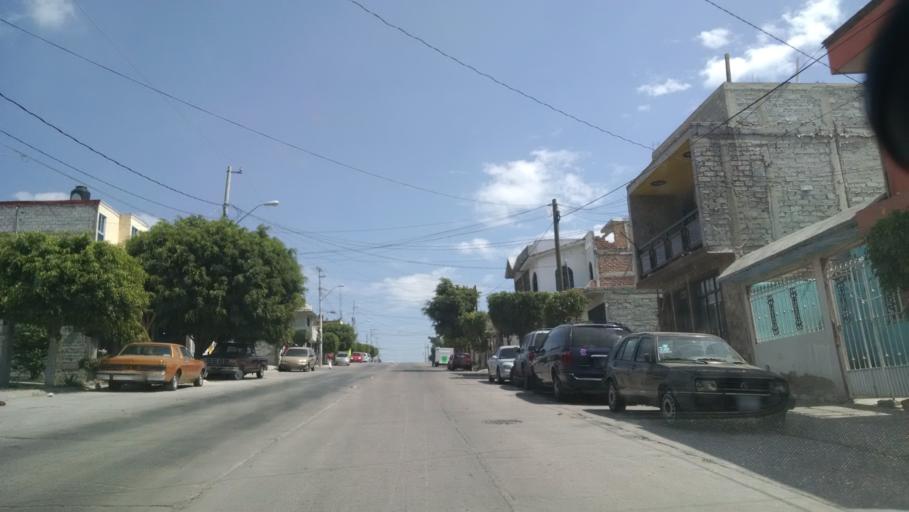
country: MX
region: Guanajuato
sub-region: Leon
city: La Ermita
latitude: 21.1535
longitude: -101.7334
